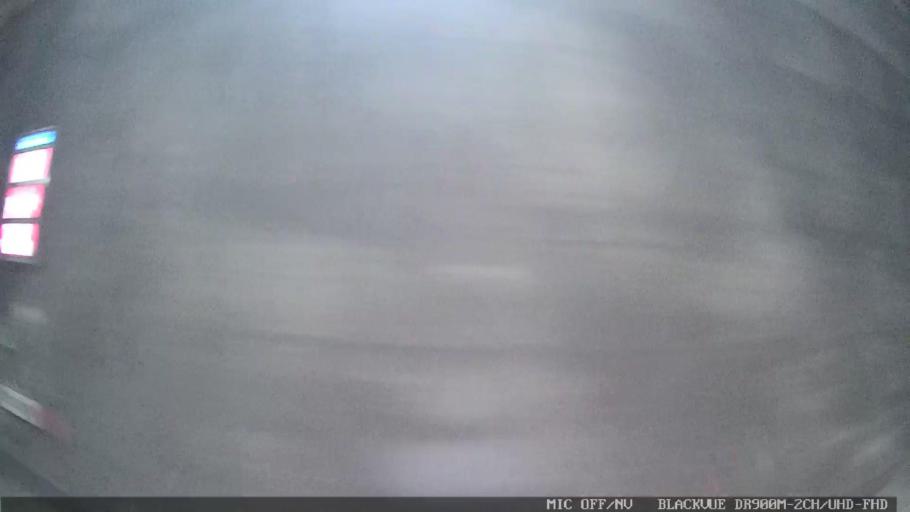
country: BR
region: Sao Paulo
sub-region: Cubatao
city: Cubatao
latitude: -23.8800
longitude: -46.4848
